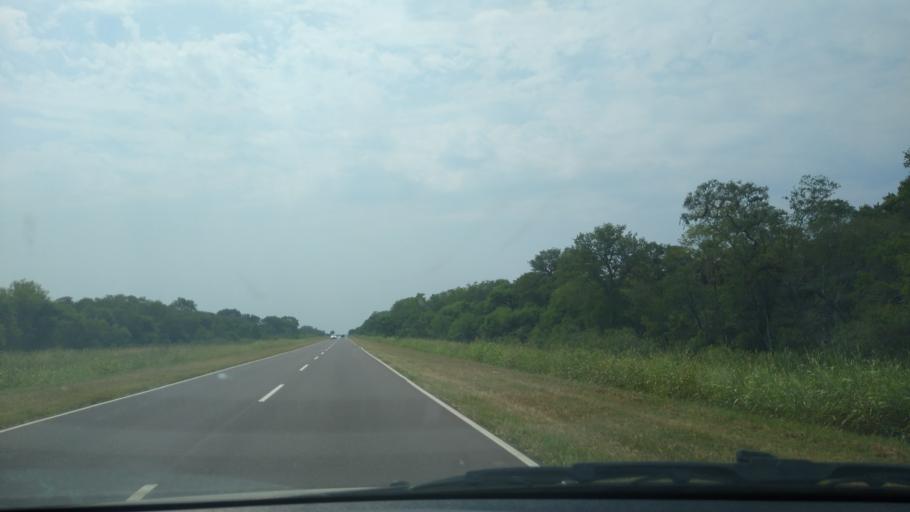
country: AR
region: Chaco
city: La Eduvigis
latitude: -27.0154
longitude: -58.9693
